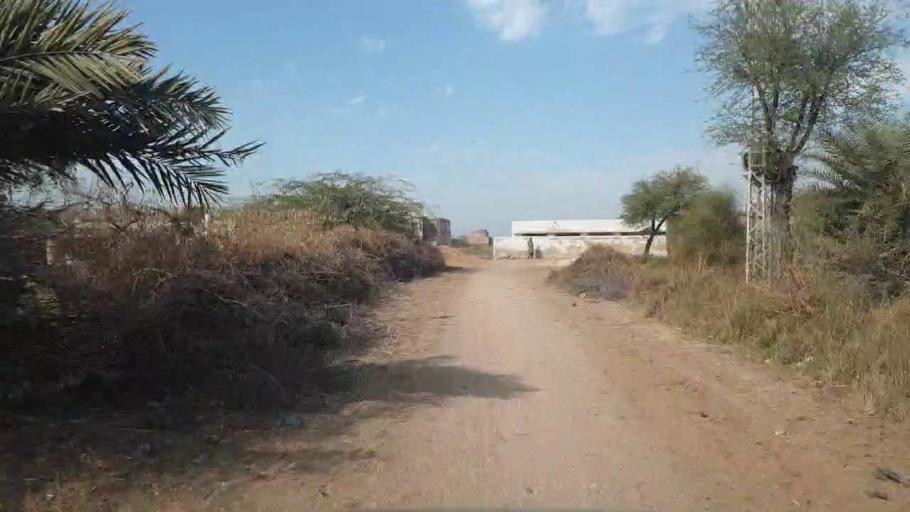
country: PK
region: Sindh
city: Sakrand
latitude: 26.0215
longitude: 68.4170
